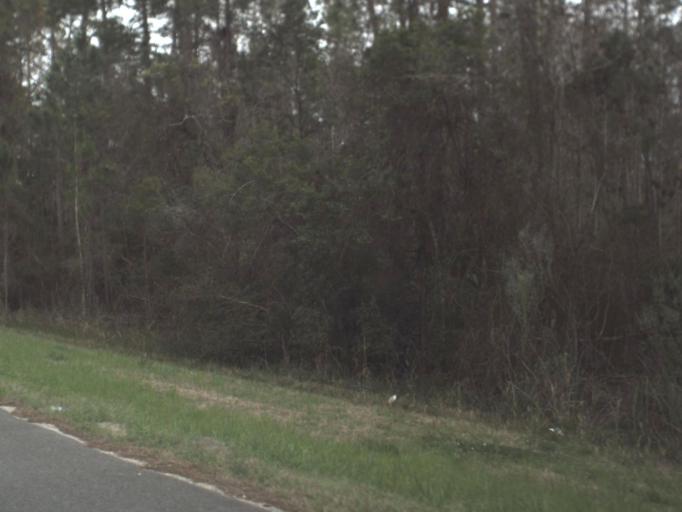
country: US
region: Florida
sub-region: Leon County
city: Woodville
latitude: 30.1910
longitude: -84.0727
